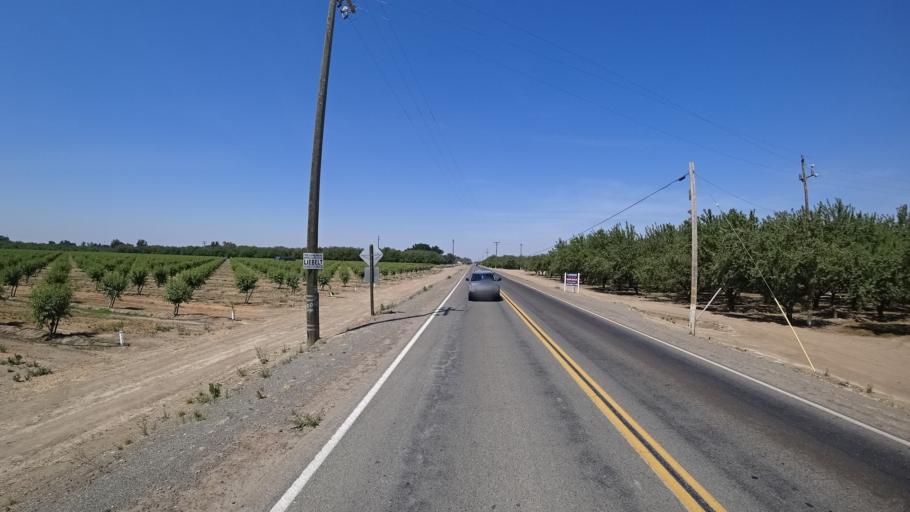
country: US
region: California
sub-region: Fresno County
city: Laton
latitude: 36.4020
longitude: -119.7557
